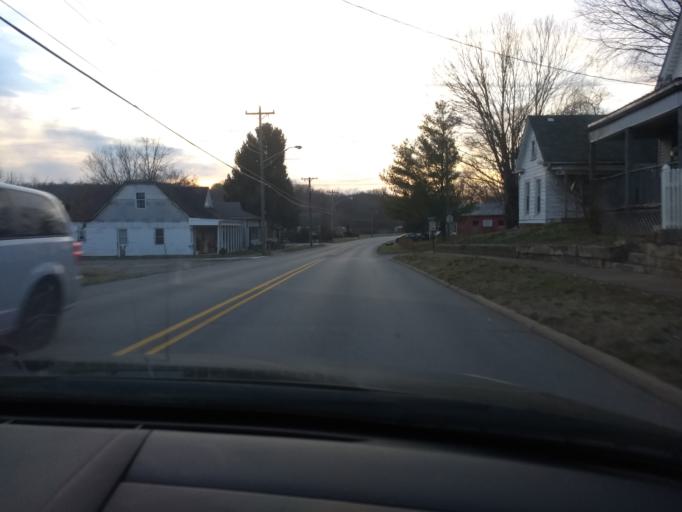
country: US
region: Indiana
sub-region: Floyd County
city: Georgetown
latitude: 38.2945
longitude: -85.9788
